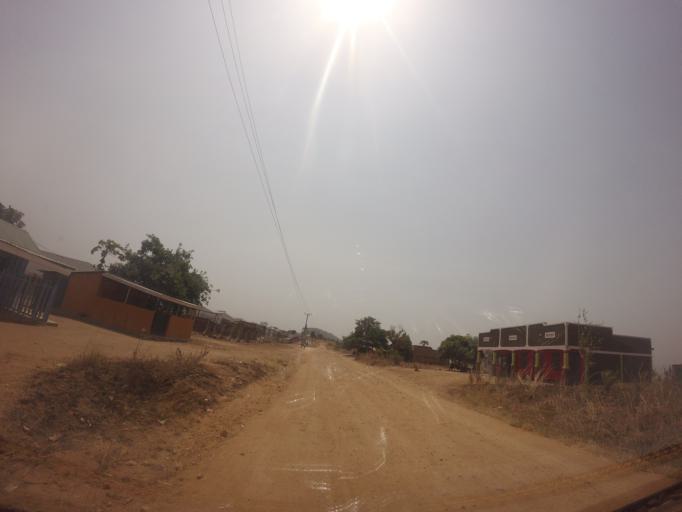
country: UG
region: Northern Region
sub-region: Arua District
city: Arua
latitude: 2.9364
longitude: 30.9816
